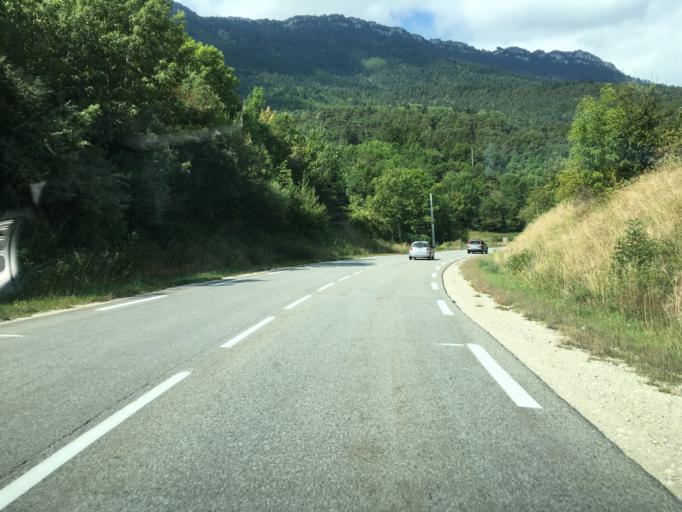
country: FR
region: Rhone-Alpes
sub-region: Departement de l'Isere
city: Mens
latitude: 44.8035
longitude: 5.6320
